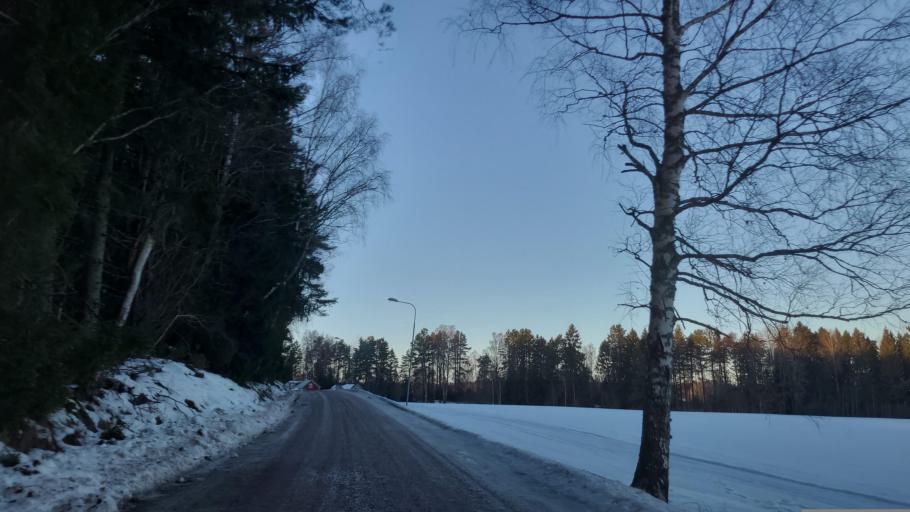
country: SE
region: Gaevleborg
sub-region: Soderhamns Kommun
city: Soderhamn
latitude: 61.2764
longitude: 16.9888
